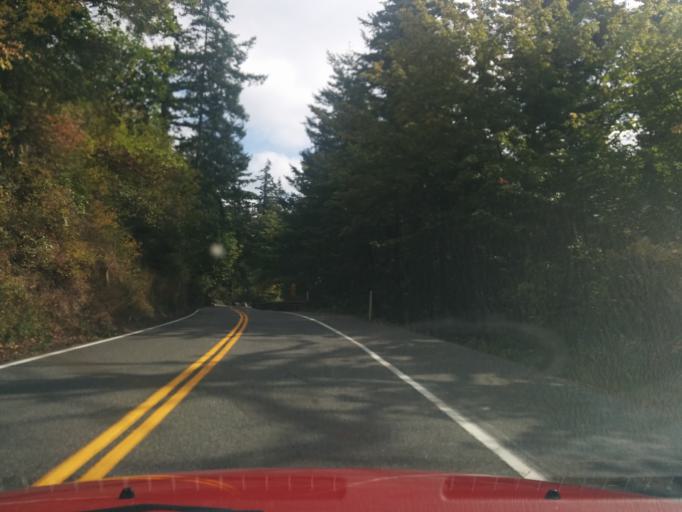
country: US
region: Washington
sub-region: Whatcom County
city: Geneva
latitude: 48.6279
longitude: -122.4646
